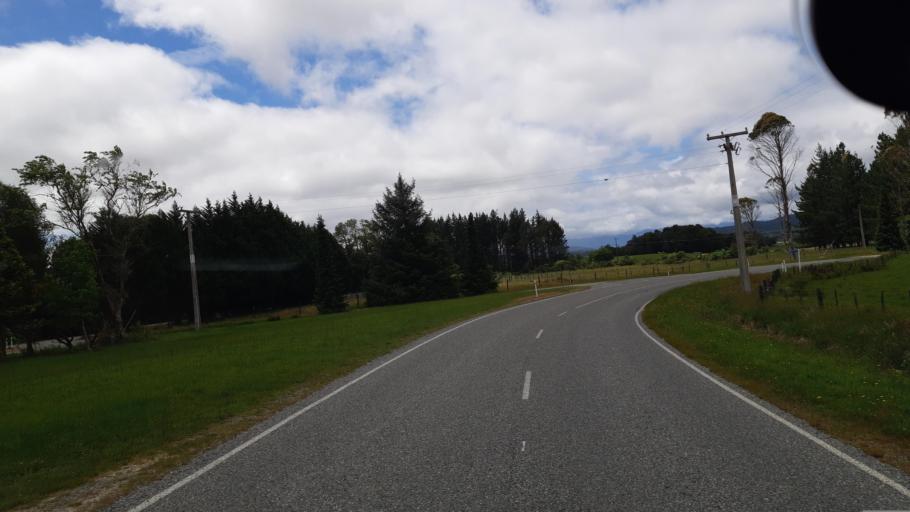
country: NZ
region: West Coast
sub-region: Grey District
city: Greymouth
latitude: -42.3356
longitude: 171.4844
